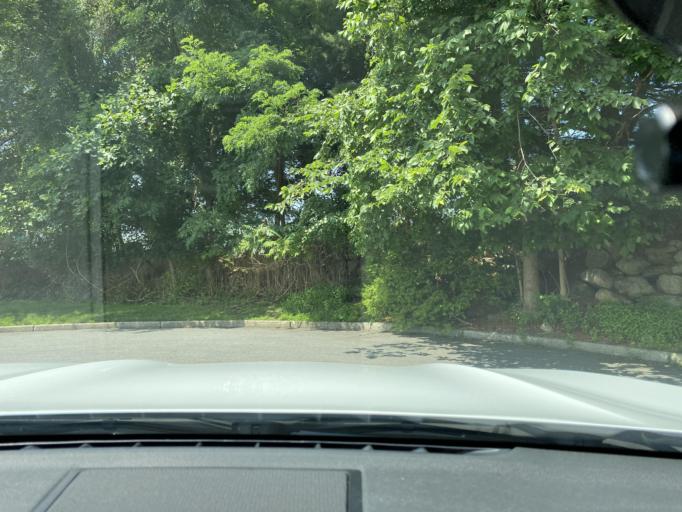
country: US
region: New York
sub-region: Rockland County
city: Airmont
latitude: 41.0901
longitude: -74.1229
